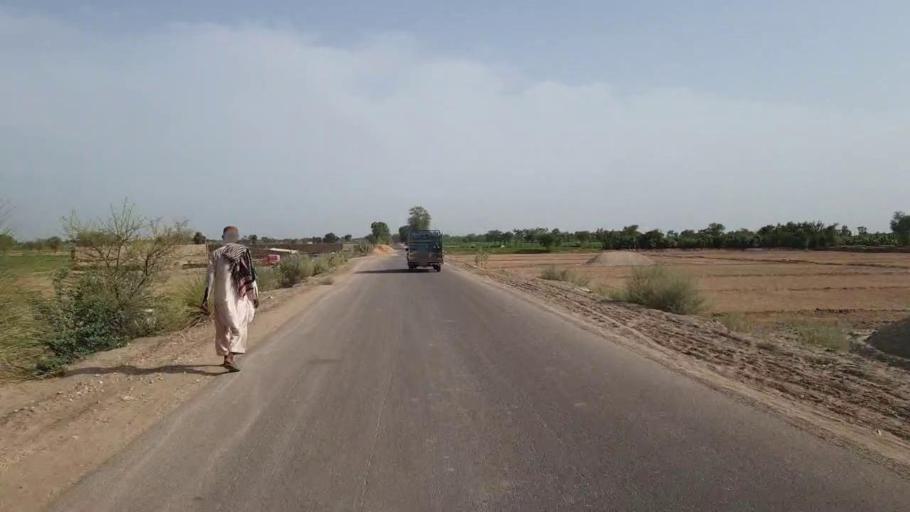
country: PK
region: Sindh
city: Sakrand
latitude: 26.2604
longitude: 68.2849
